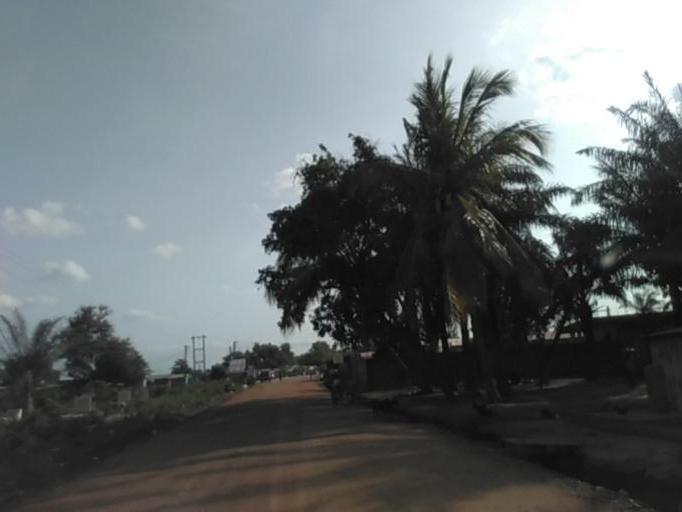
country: GH
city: Akropong
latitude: 6.0923
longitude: 0.1974
